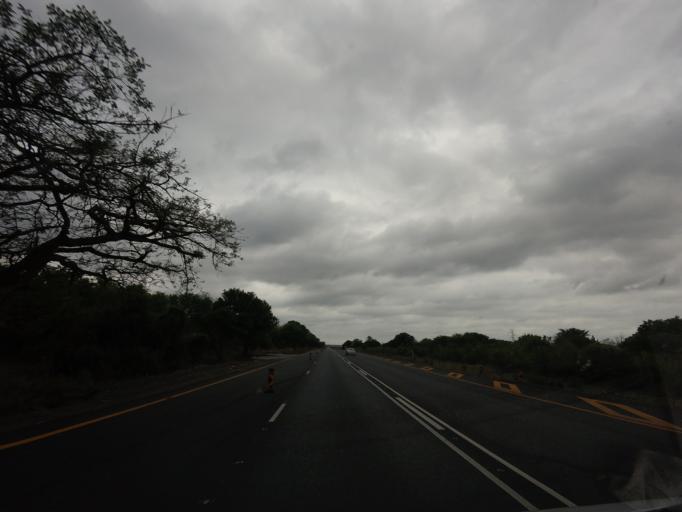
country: ZA
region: Mpumalanga
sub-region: Ehlanzeni District
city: Komatipoort
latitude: -25.4367
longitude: 31.8054
